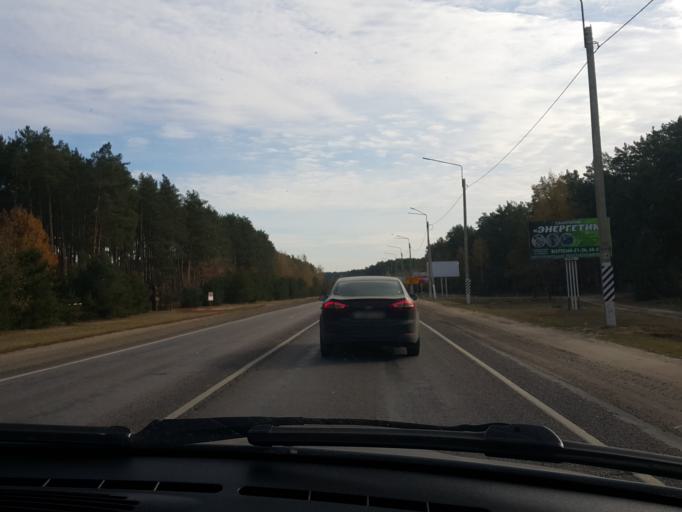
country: RU
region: Tambov
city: Donskoye
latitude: 52.7127
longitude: 41.5211
